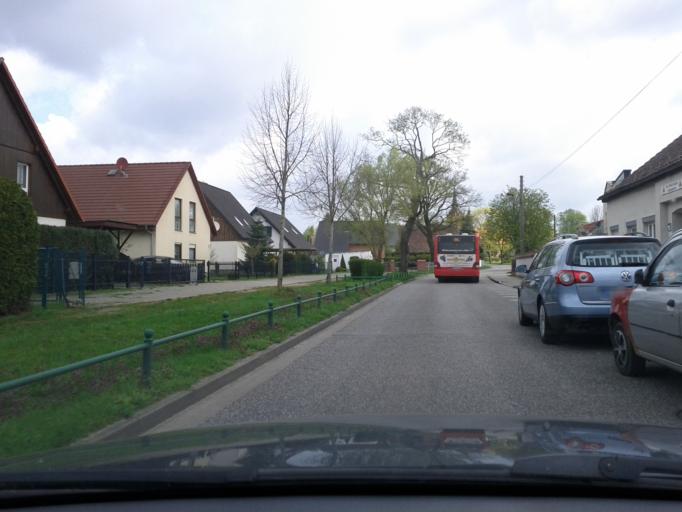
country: DE
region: Brandenburg
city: Schoneiche
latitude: 52.4894
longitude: 13.6712
